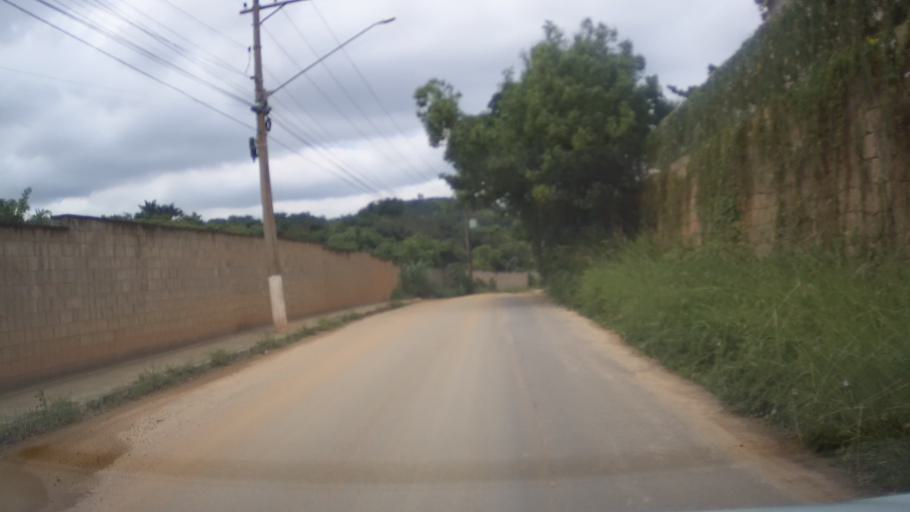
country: BR
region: Sao Paulo
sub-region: Louveira
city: Louveira
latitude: -23.0770
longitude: -46.9899
